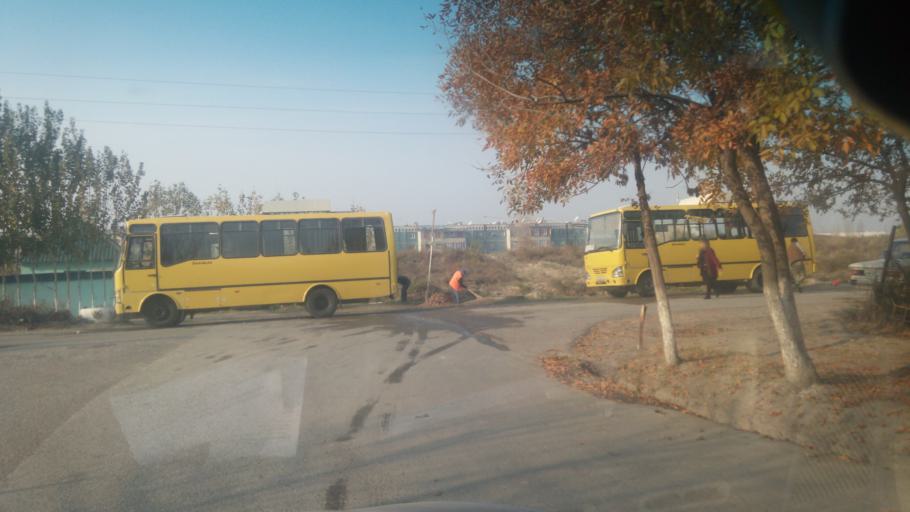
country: UZ
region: Sirdaryo
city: Guliston
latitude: 40.5180
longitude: 68.7741
